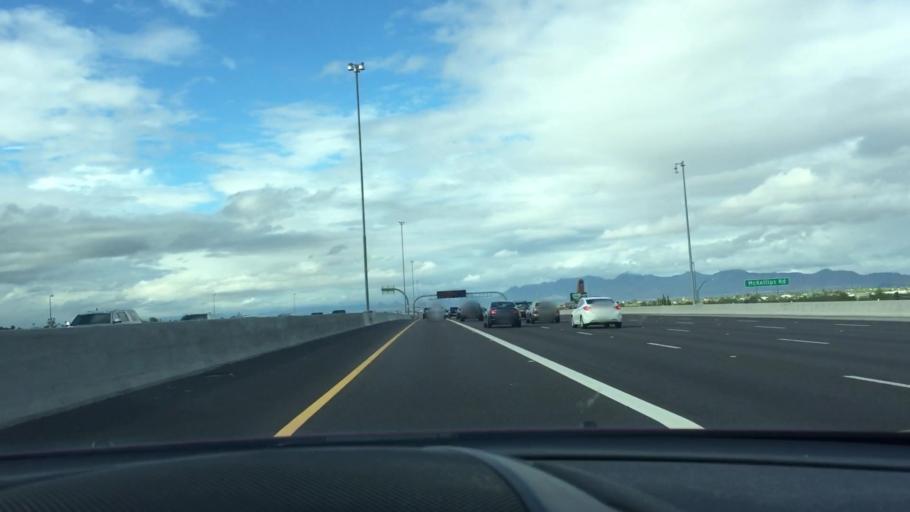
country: US
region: Arizona
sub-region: Maricopa County
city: Tempe
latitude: 33.4508
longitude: -111.8892
